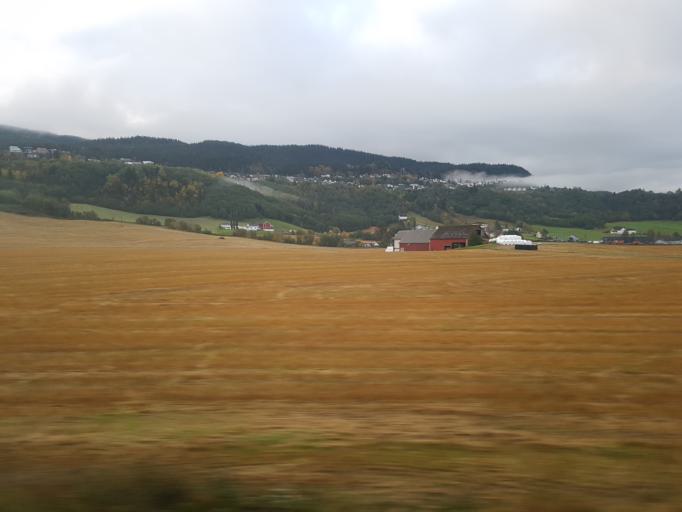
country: NO
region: Sor-Trondelag
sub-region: Melhus
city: Melhus
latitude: 63.3035
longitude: 10.2902
